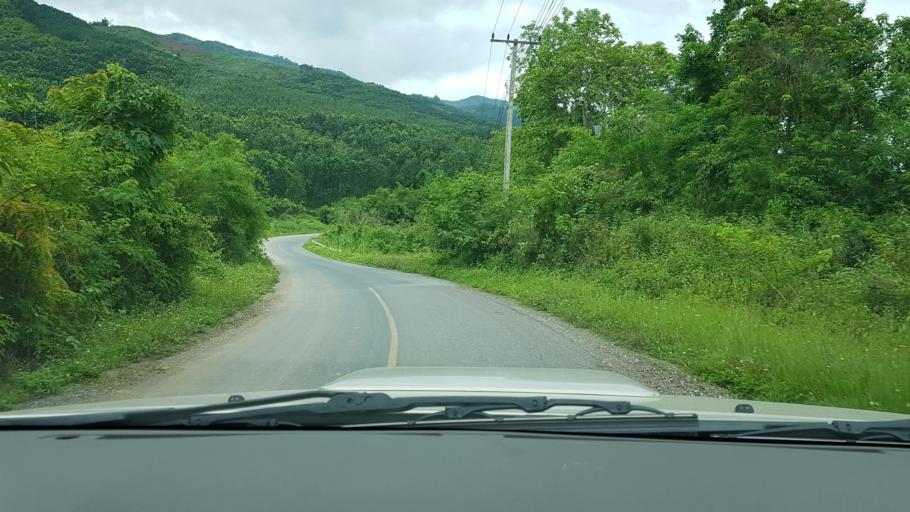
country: LA
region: Loungnamtha
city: Muang Nale
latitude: 20.2431
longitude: 101.5767
